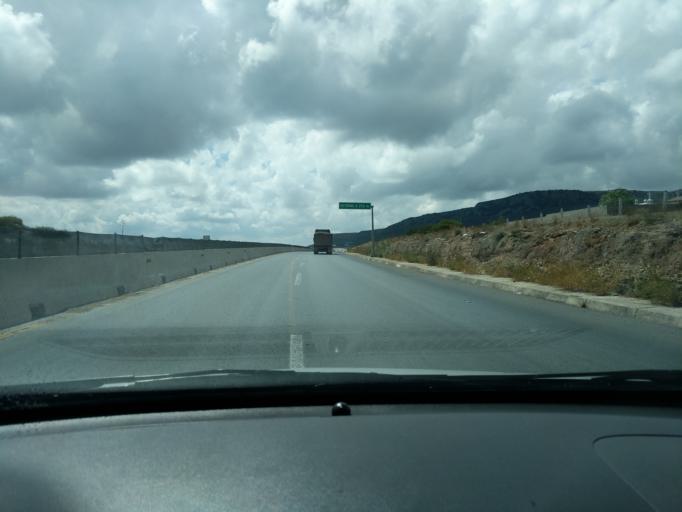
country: MX
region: Zacatecas
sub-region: Pinos
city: Santiago
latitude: 22.4063
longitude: -101.3910
